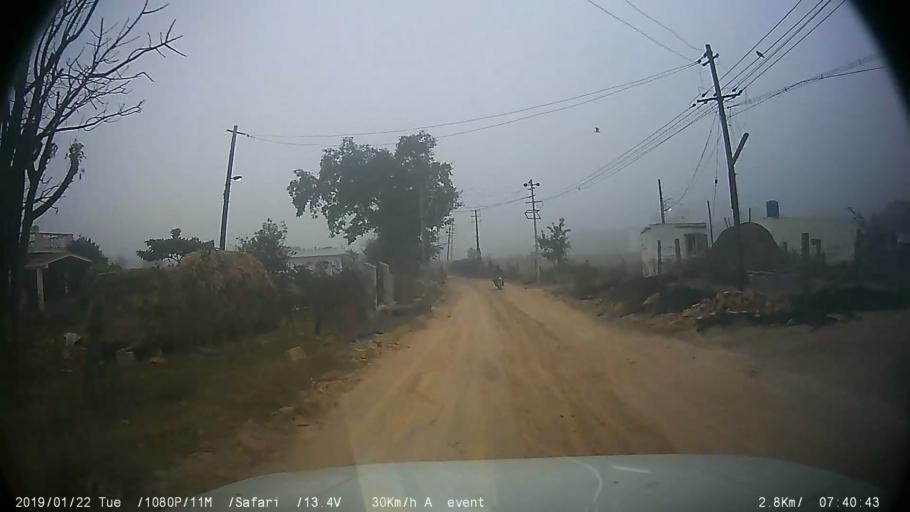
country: IN
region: Karnataka
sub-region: Bangalore Urban
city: Anekal
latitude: 12.8206
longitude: 77.6374
